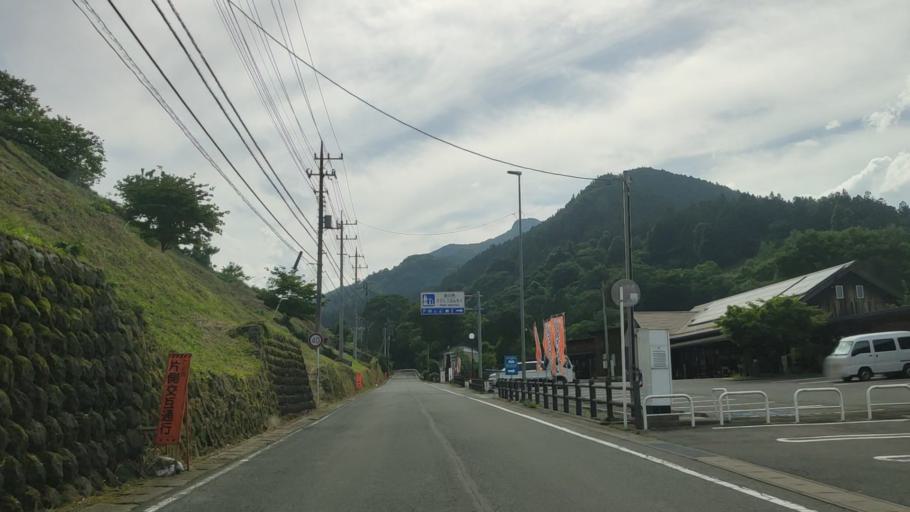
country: JP
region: Gunma
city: Tomioka
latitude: 36.1778
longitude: 138.7417
